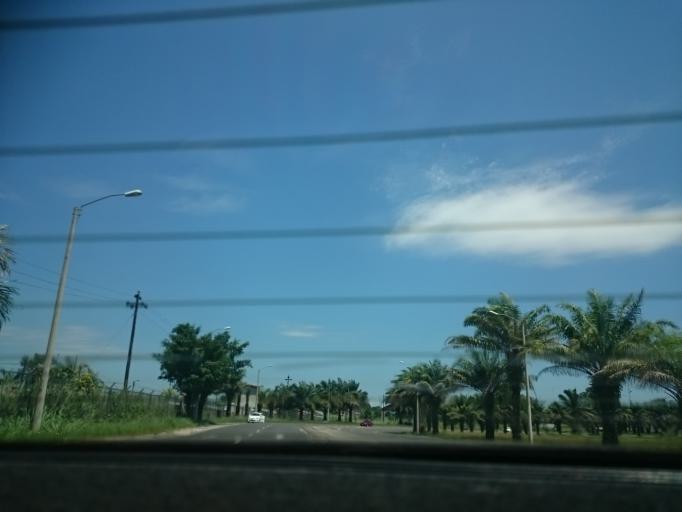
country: PE
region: Loreto
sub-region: Provincia de Maynas
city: Iquitos
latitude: -3.7855
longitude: -73.3004
